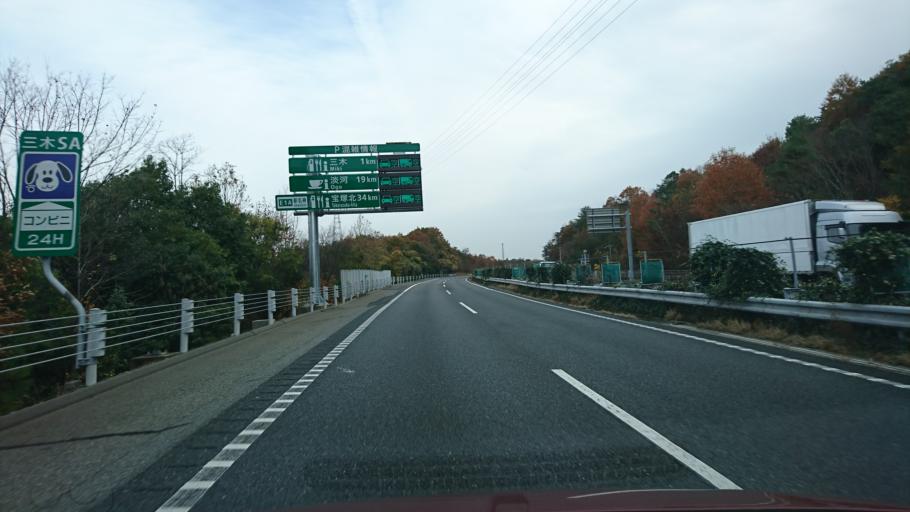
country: JP
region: Hyogo
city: Miki
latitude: 34.8163
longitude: 134.9665
